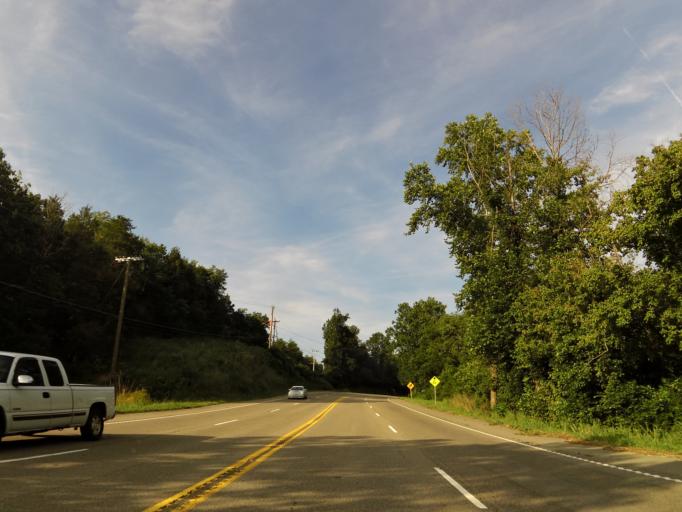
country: US
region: Tennessee
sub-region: Sevier County
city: Seymour
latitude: 35.8645
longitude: -83.6634
